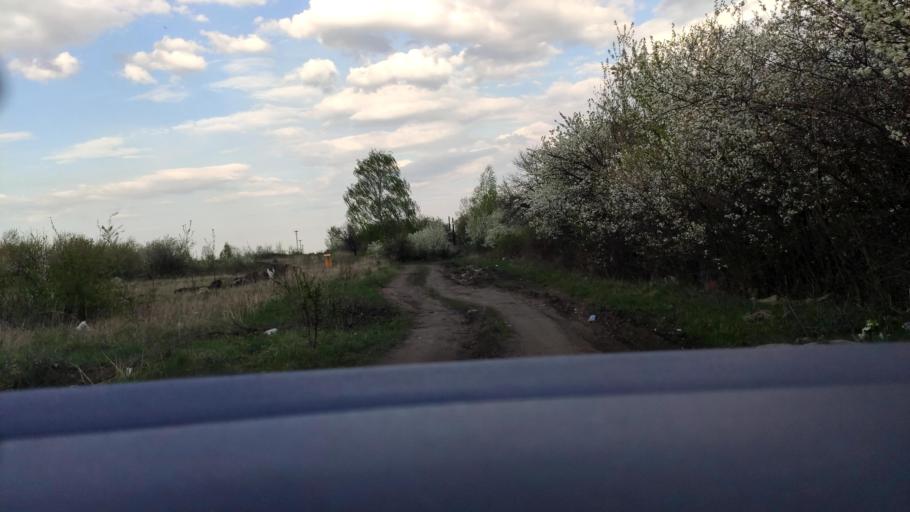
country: RU
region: Voronezj
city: Voronezh
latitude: 51.6087
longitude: 39.1488
